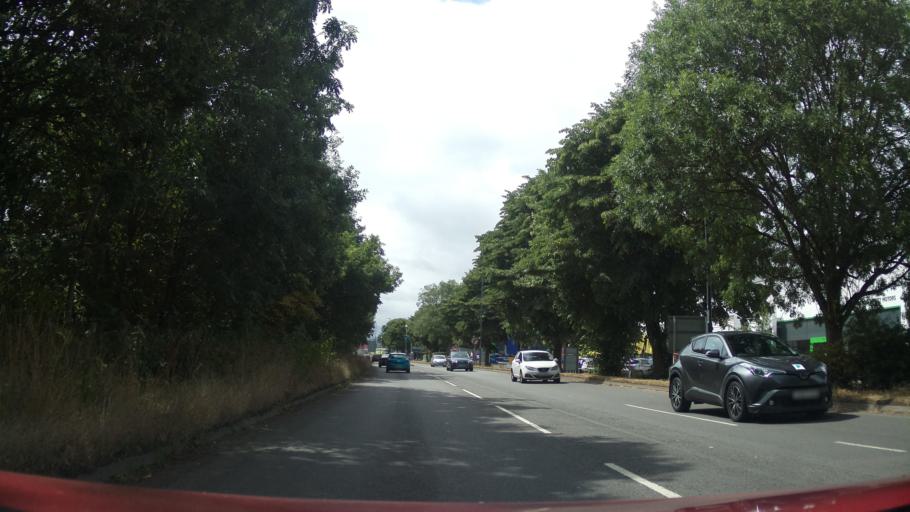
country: GB
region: England
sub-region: Derby
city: Derby
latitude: 52.9353
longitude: -1.4642
